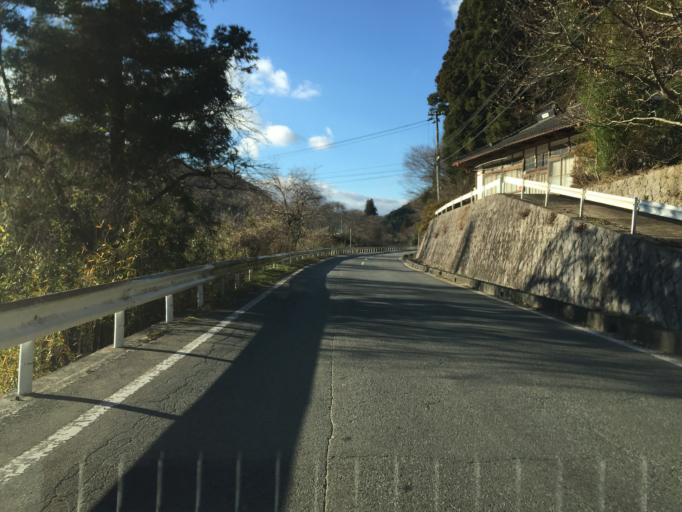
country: JP
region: Fukushima
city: Iwaki
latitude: 37.2055
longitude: 140.7545
